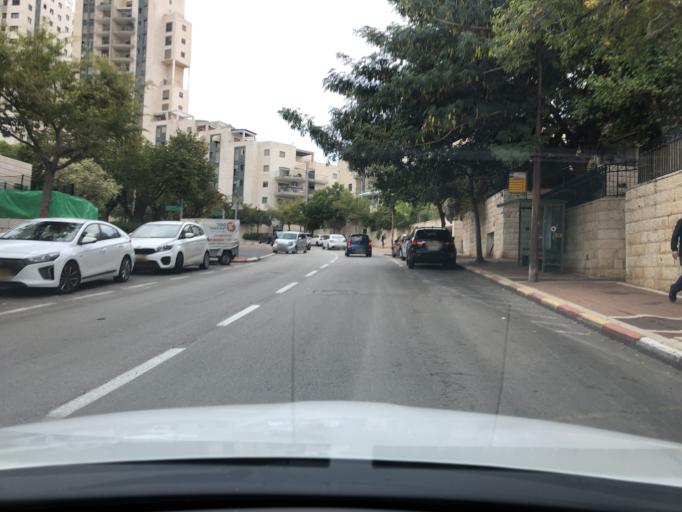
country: IL
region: Central District
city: Modiin
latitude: 31.9056
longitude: 35.0111
